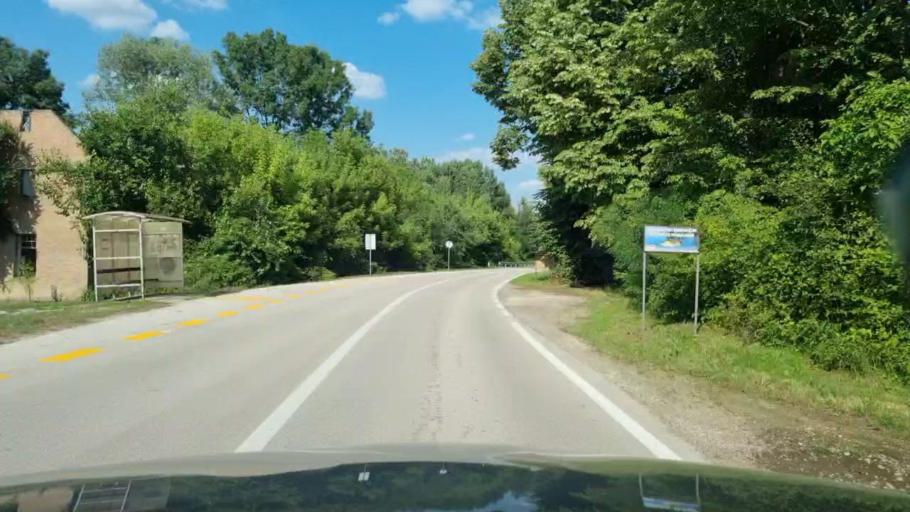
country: HR
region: Brodsko-Posavska
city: Garcin
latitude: 45.0779
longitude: 18.1990
